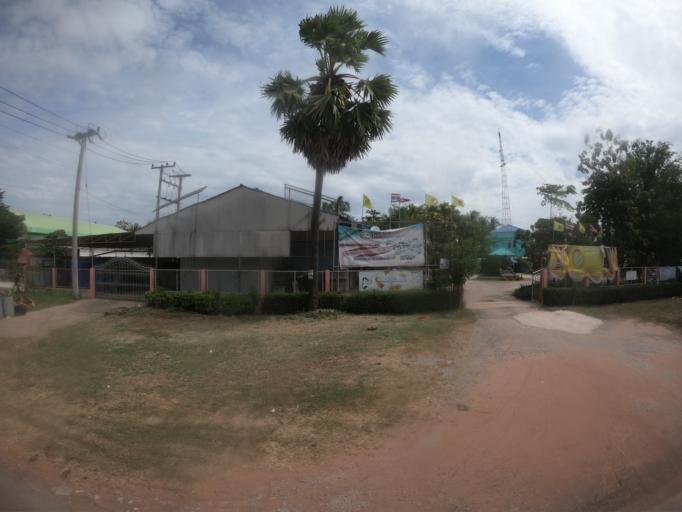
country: TH
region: Maha Sarakham
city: Chiang Yuen
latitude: 16.3859
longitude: 103.1024
